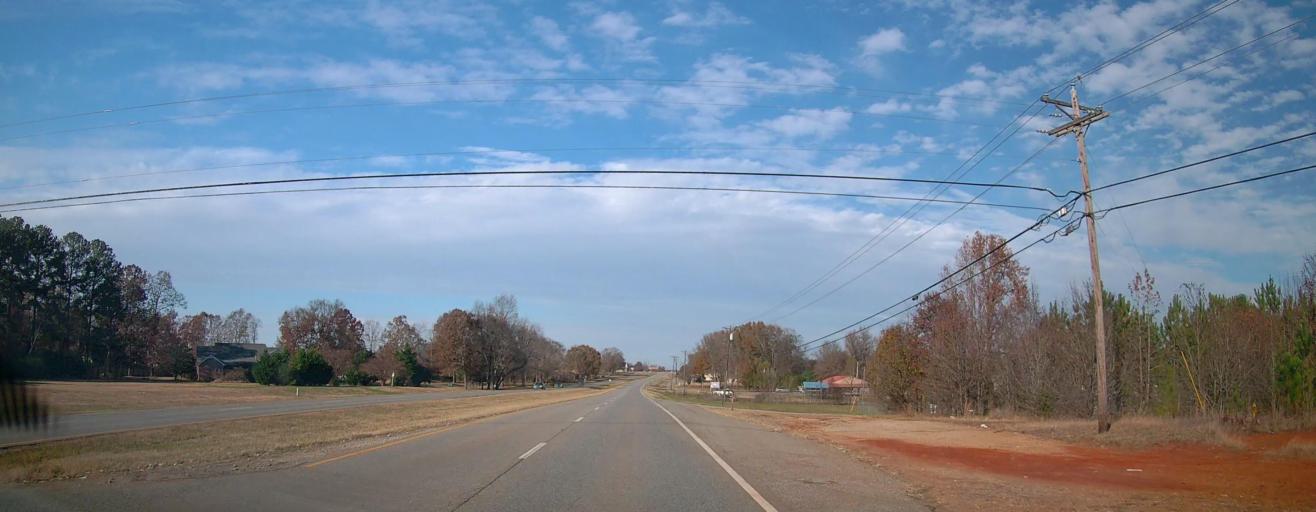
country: US
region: Alabama
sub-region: Limestone County
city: Athens
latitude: 34.7216
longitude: -86.9567
